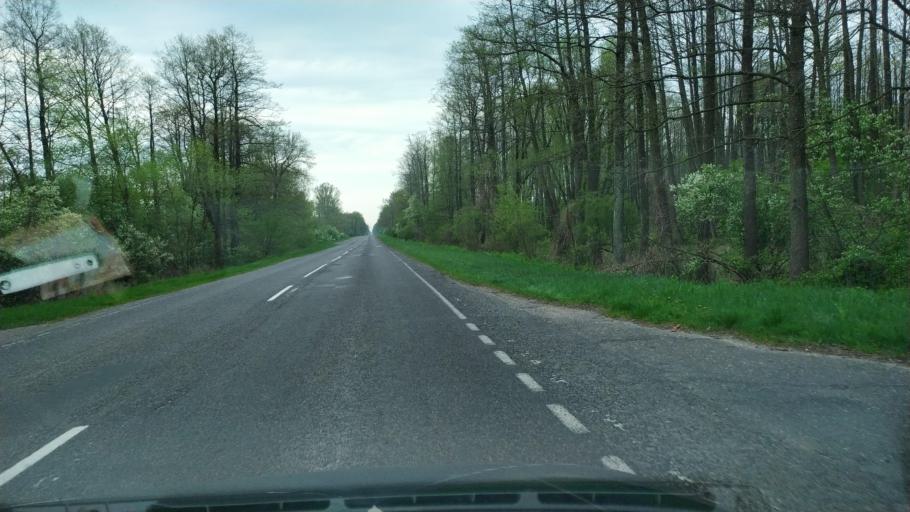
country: BY
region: Brest
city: Zhabinka
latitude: 52.2904
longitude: 23.9414
